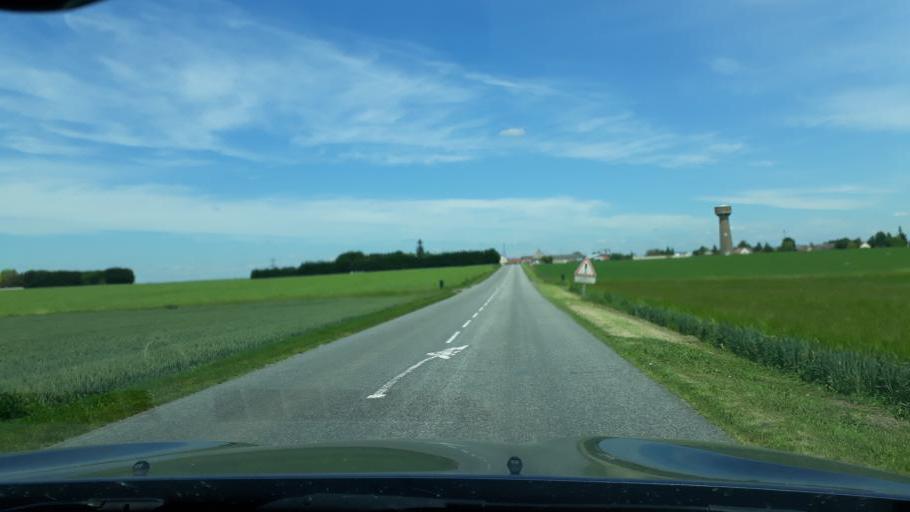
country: FR
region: Centre
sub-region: Departement du Loiret
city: Dadonville
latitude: 48.0970
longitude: 2.2701
